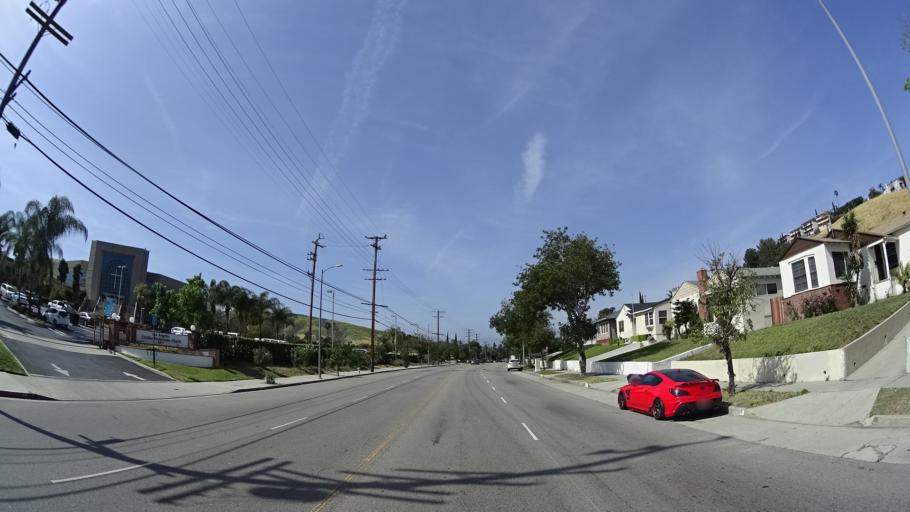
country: US
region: California
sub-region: Los Angeles County
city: Belvedere
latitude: 34.0708
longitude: -118.1806
